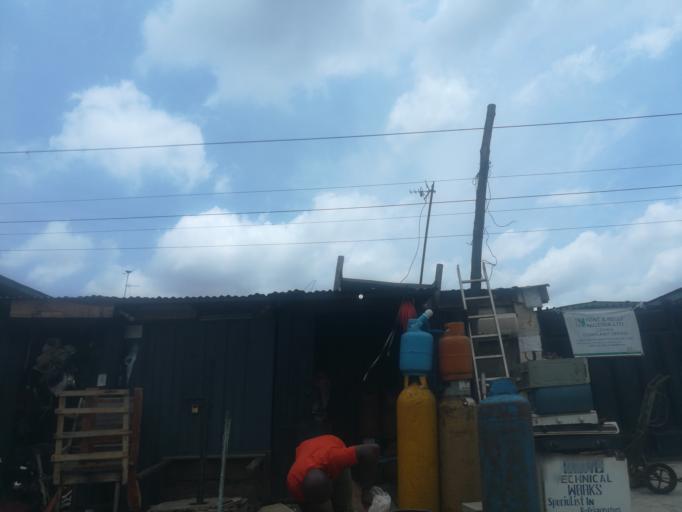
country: NG
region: Lagos
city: Ojota
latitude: 6.5622
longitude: 3.3909
